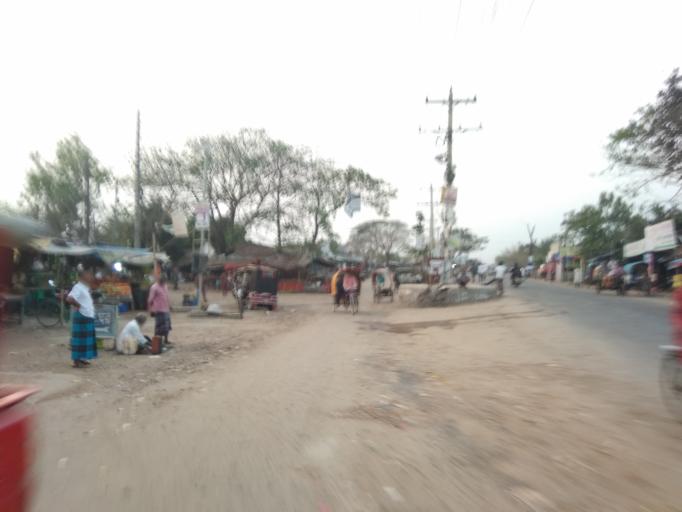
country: IN
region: West Bengal
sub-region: North 24 Parganas
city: Taki
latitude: 22.4540
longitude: 89.0345
